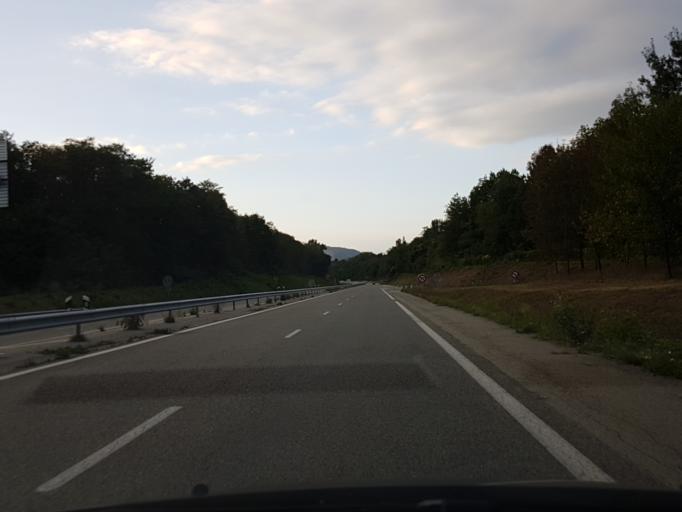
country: FR
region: Midi-Pyrenees
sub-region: Departement de l'Ariege
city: Montgaillard
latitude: 42.9227
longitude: 1.6358
